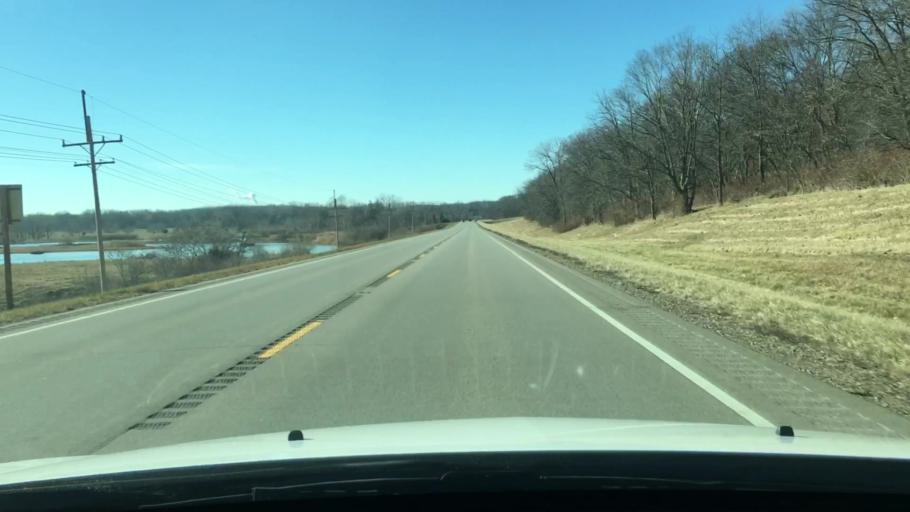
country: US
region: Illinois
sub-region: Peoria County
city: Glasford
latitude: 40.5204
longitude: -89.8902
